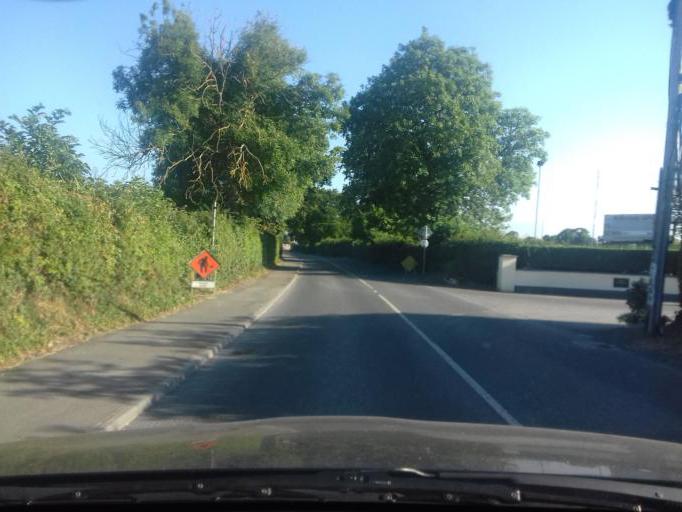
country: IE
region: Leinster
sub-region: An Mhi
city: Ashbourne
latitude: 53.4542
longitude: -6.3957
